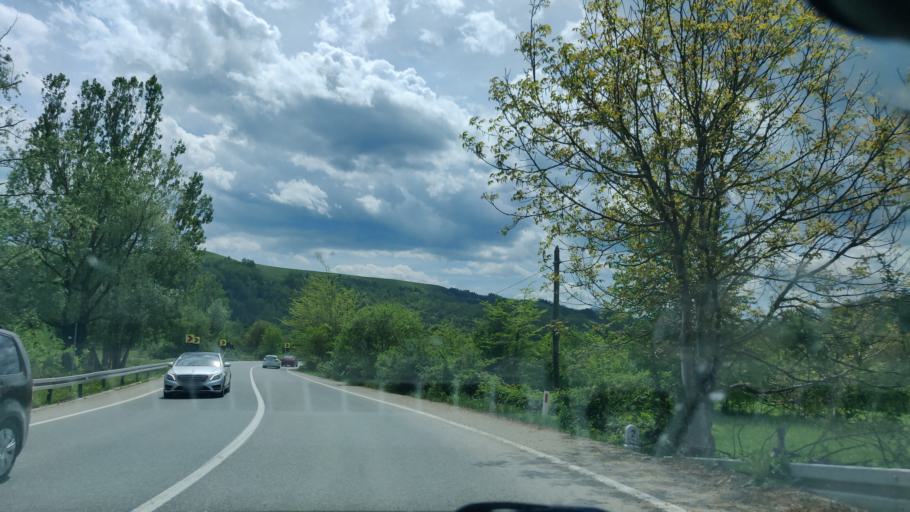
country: RO
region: Vrancea
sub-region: Comuna Negrilesti
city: Negrilesti
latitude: 45.9248
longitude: 26.7109
